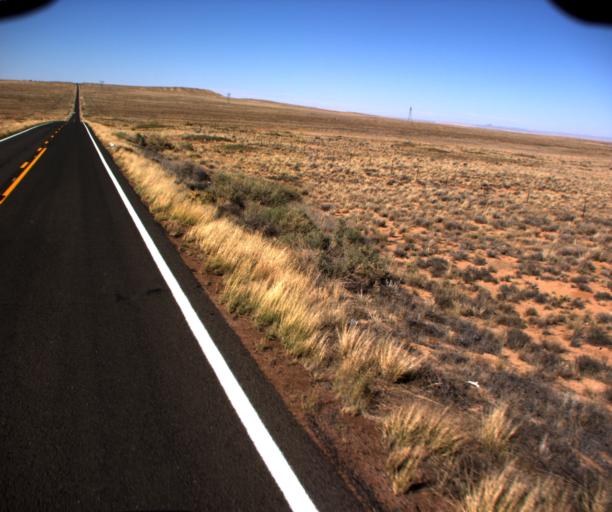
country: US
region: Arizona
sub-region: Coconino County
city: Tuba City
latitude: 35.9406
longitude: -110.9071
